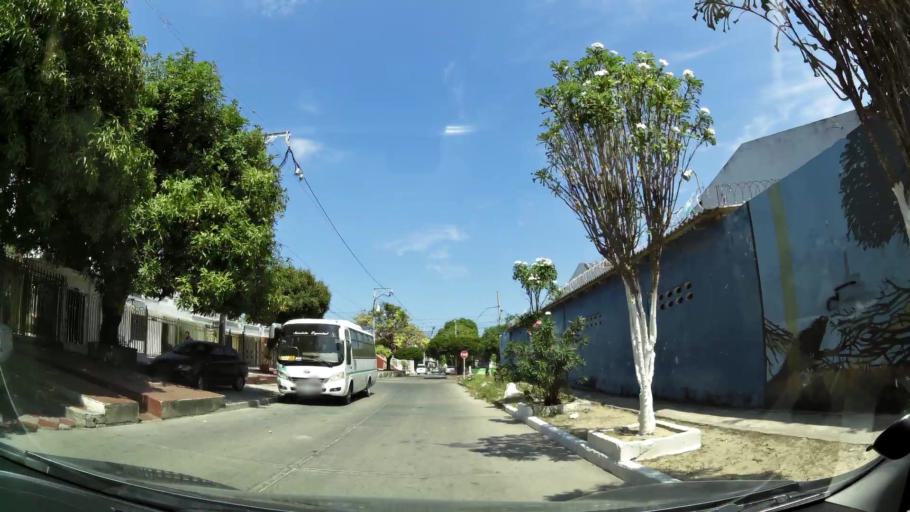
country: CO
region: Atlantico
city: Barranquilla
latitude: 10.9576
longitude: -74.8056
